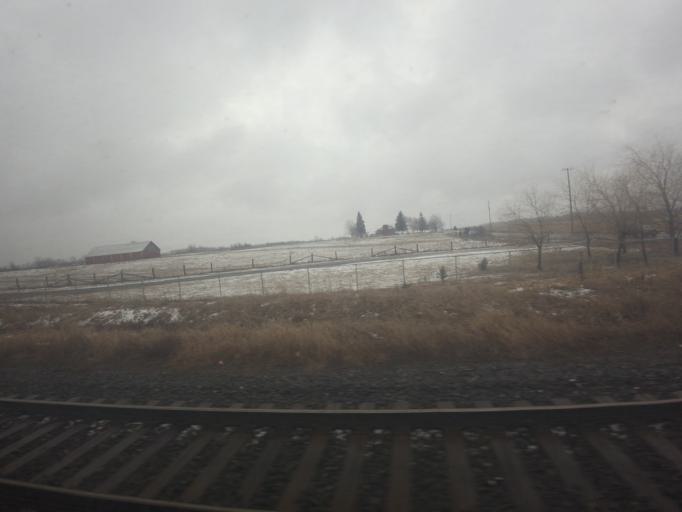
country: CA
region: Ontario
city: Belleville
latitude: 44.2006
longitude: -77.2898
